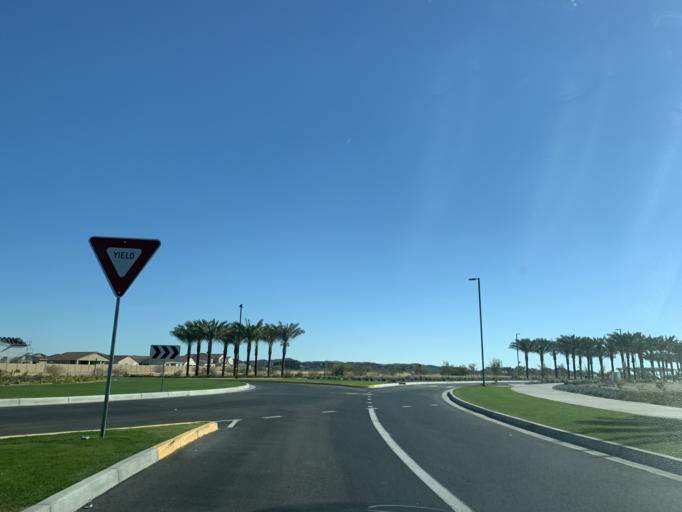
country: US
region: Arizona
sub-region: Maricopa County
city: Queen Creek
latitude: 33.3197
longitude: -111.6320
